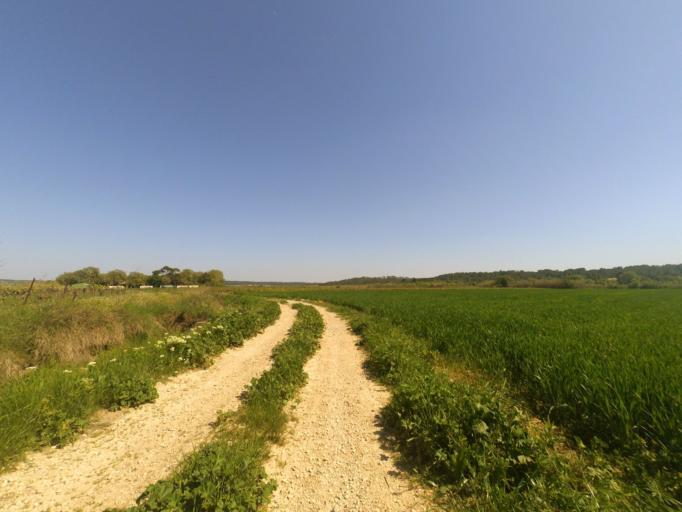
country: FR
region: Languedoc-Roussillon
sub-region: Departement du Gard
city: Congenies
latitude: 43.7705
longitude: 4.1783
